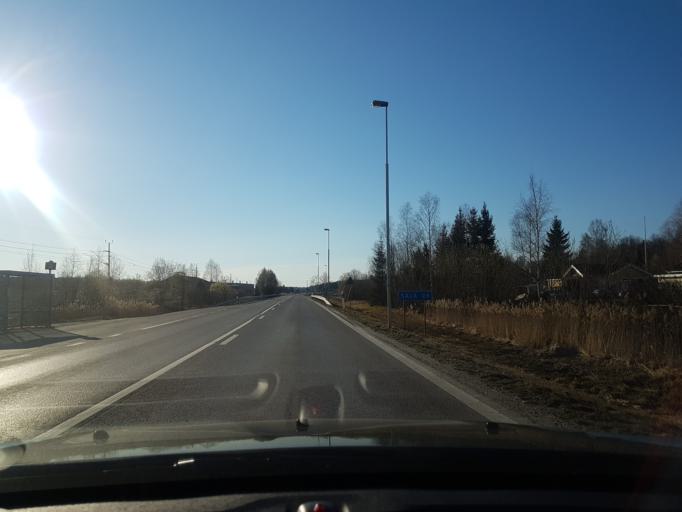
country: SE
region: Uppsala
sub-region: Heby Kommun
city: Morgongava
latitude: 59.9047
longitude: 17.0546
